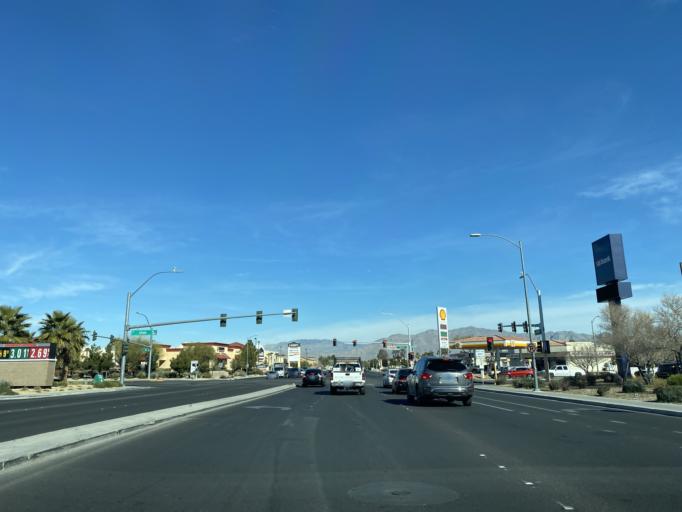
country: US
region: Nevada
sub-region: Clark County
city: Las Vegas
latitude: 36.2384
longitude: -115.2254
